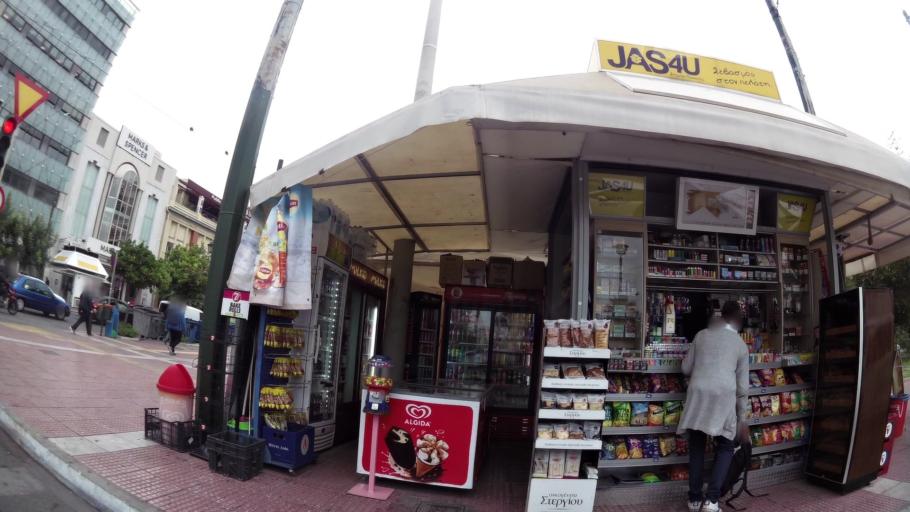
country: GR
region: Attica
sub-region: Nomos Attikis
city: Piraeus
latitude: 37.9394
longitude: 23.6488
